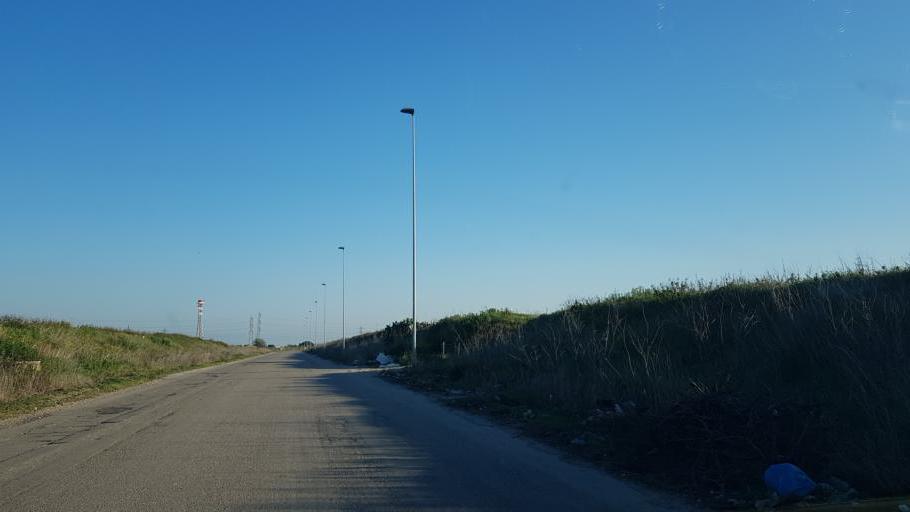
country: IT
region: Apulia
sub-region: Provincia di Brindisi
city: La Rosa
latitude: 40.6209
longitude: 17.9704
